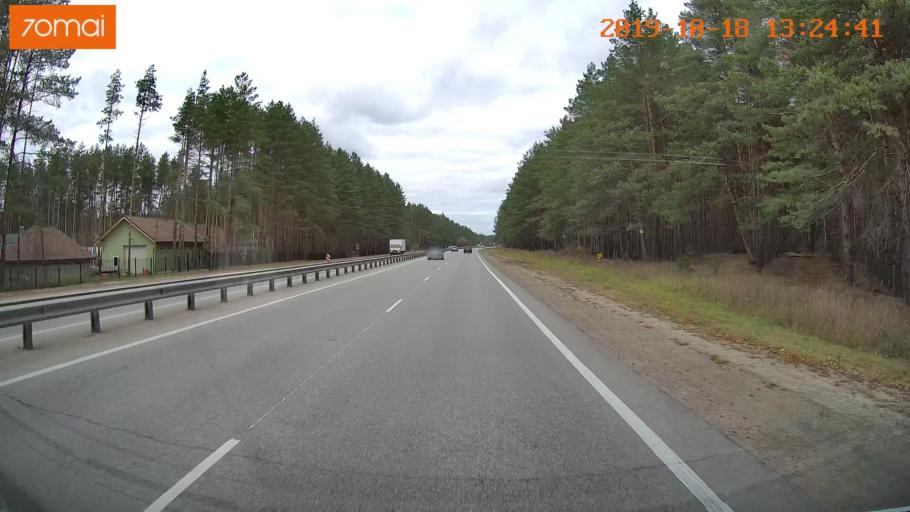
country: RU
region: Rjazan
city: Polyany
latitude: 54.7344
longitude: 39.8423
